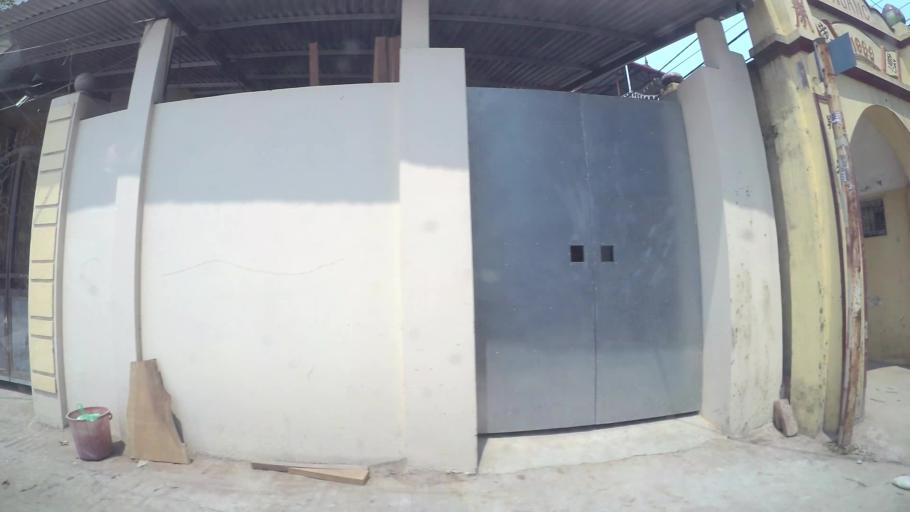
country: VN
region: Ha Noi
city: Van Dien
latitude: 20.9516
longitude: 105.8294
